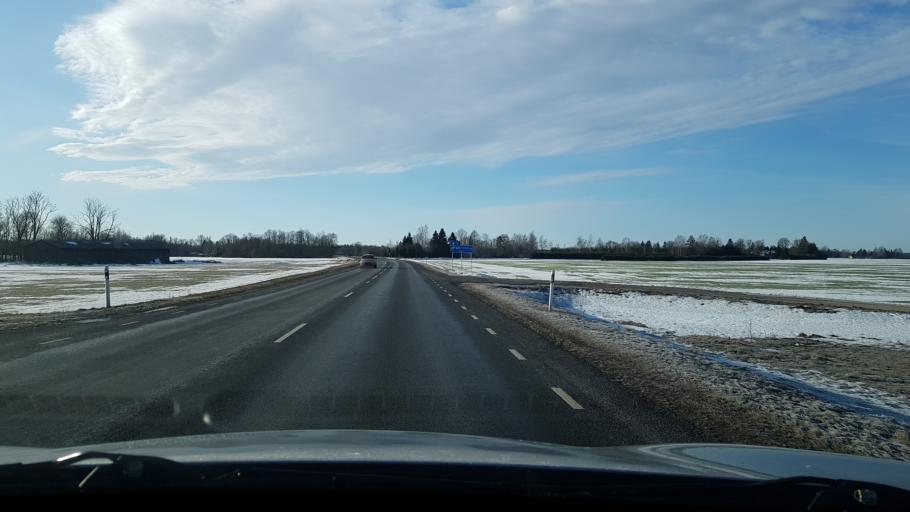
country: EE
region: Viljandimaa
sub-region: Vohma linn
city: Vohma
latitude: 58.6445
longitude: 25.5801
